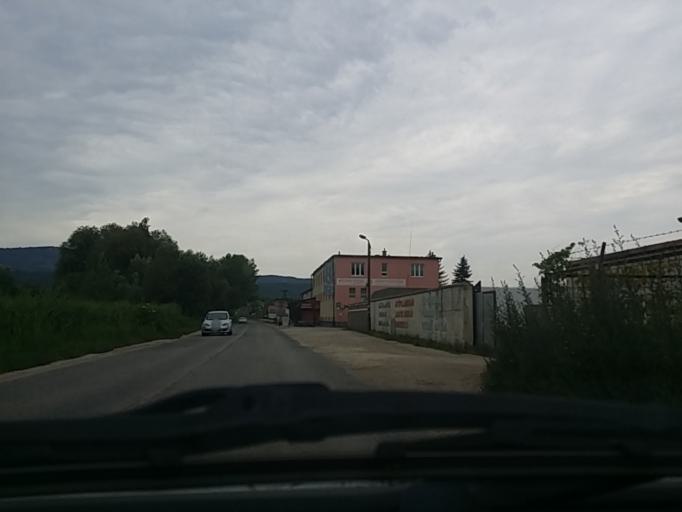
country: HU
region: Pest
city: Solymar
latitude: 47.5964
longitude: 18.9510
